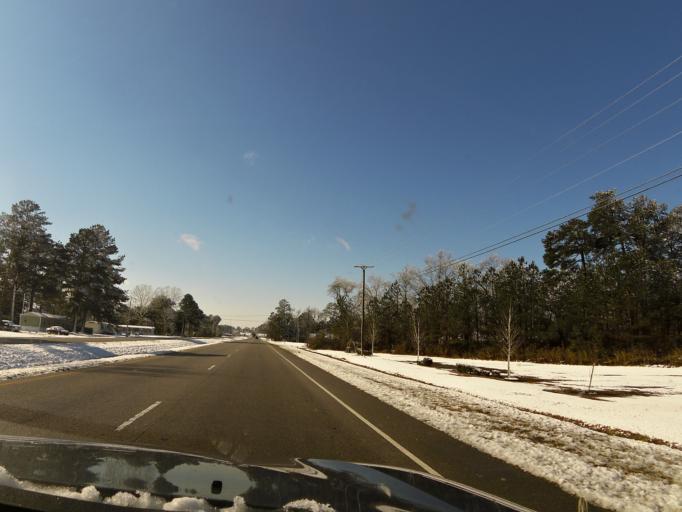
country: US
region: North Carolina
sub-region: Wilson County
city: Elm City
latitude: 35.7526
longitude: -77.8660
